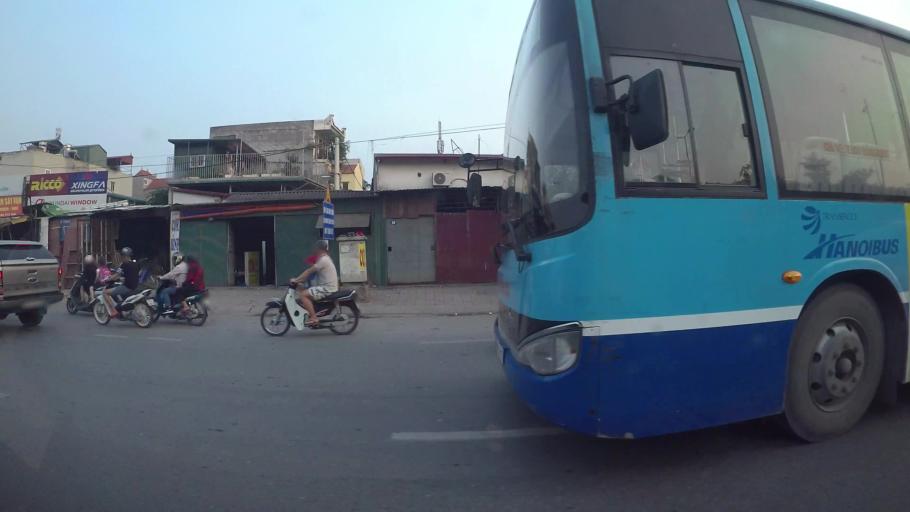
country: VN
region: Ha Noi
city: Van Dien
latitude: 20.9638
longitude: 105.8681
